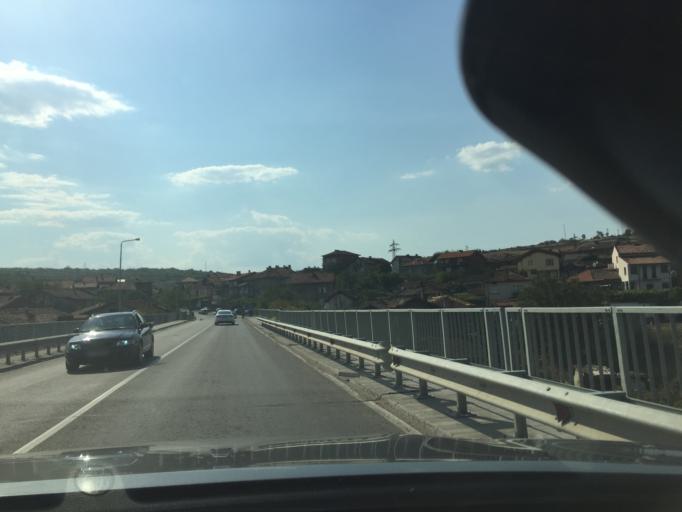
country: BG
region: Kyustendil
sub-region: Obshtina Dupnitsa
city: Dupnitsa
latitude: 42.2528
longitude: 23.0940
